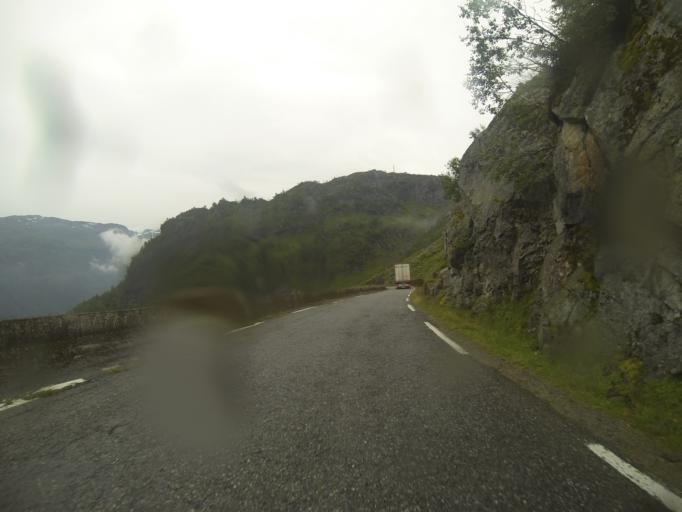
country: NO
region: Hordaland
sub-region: Odda
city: Odda
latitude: 59.7853
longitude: 6.7561
